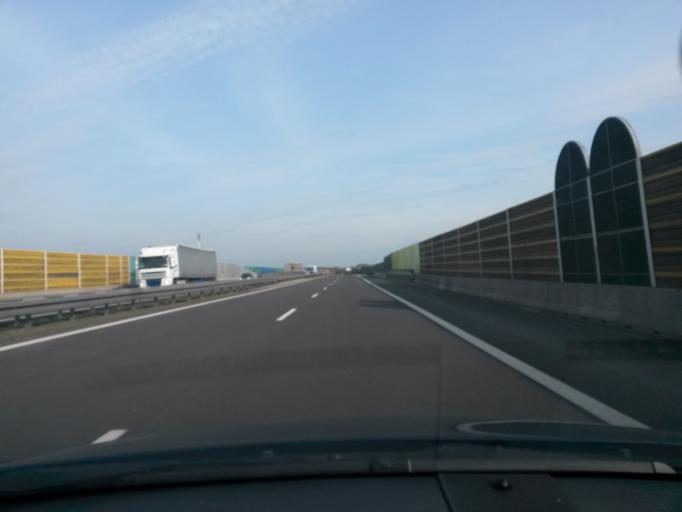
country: PL
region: Greater Poland Voivodeship
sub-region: Powiat wrzesinski
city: Wrzesnia
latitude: 52.3125
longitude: 17.5483
